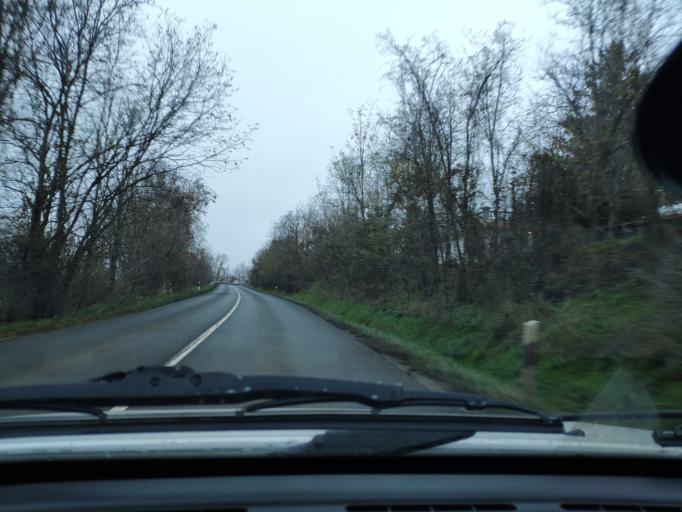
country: HU
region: Pest
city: Soskut
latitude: 47.4265
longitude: 18.8254
